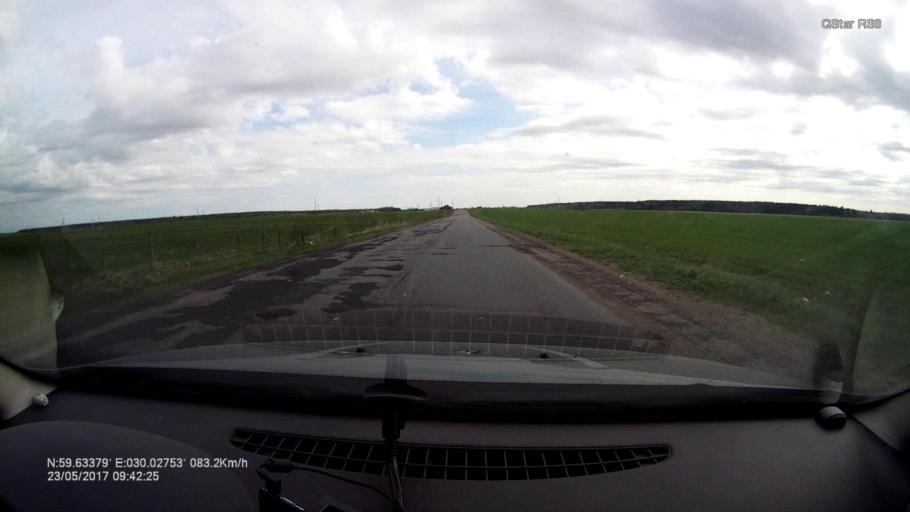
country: RU
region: Leningrad
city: Mariyenburg
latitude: 59.6340
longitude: 30.0280
